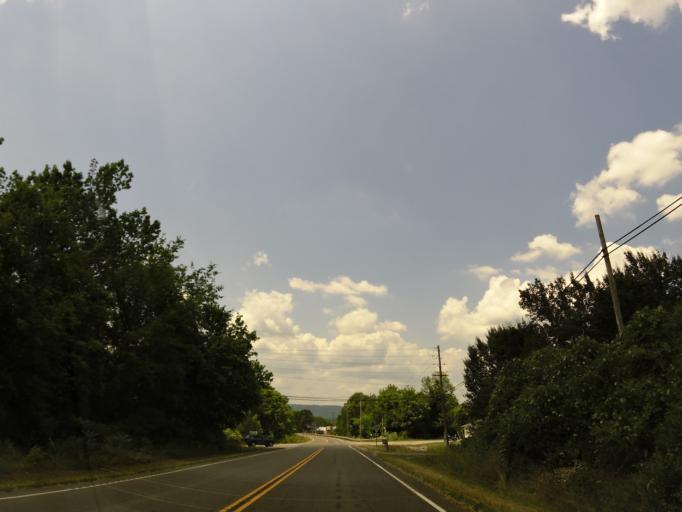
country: US
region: Tennessee
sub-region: Rhea County
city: Spring City
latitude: 35.6421
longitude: -84.8445
